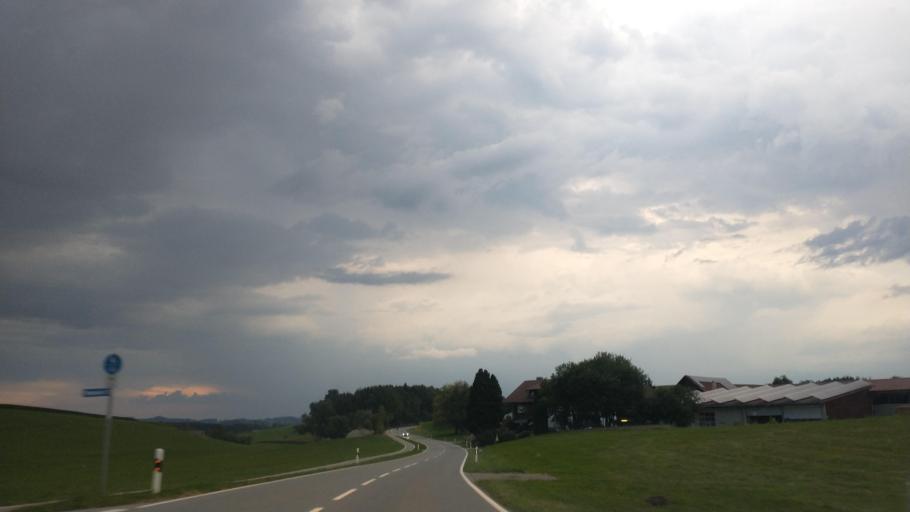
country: DE
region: Baden-Wuerttemberg
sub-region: Tuebingen Region
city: Neukirch
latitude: 47.6608
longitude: 9.7142
